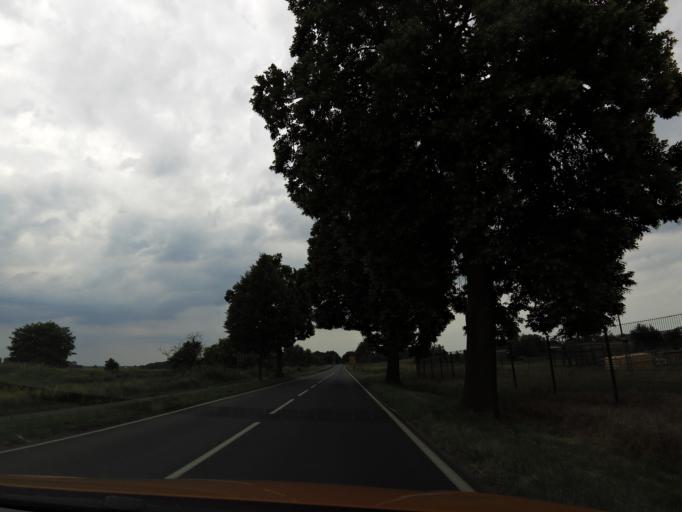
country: DE
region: Brandenburg
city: Baruth
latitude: 52.0622
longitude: 13.5081
